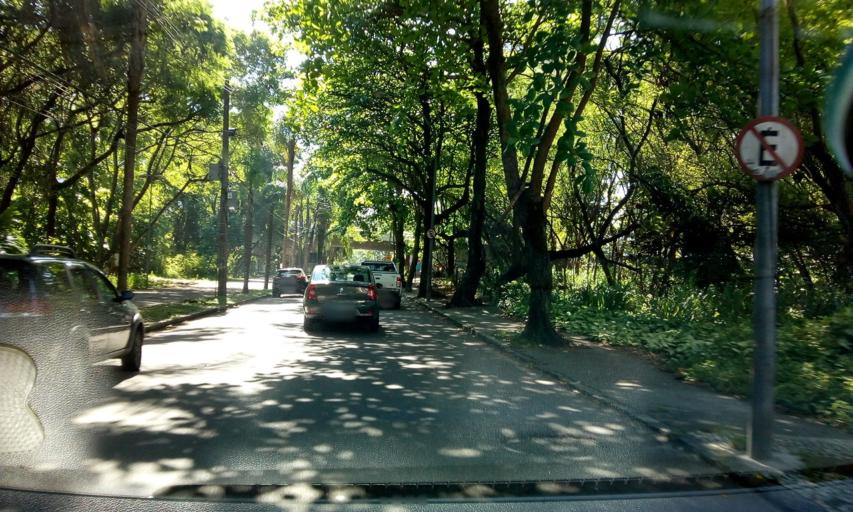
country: BR
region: Rio de Janeiro
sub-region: Rio De Janeiro
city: Rio de Janeiro
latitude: -23.0070
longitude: -43.3274
